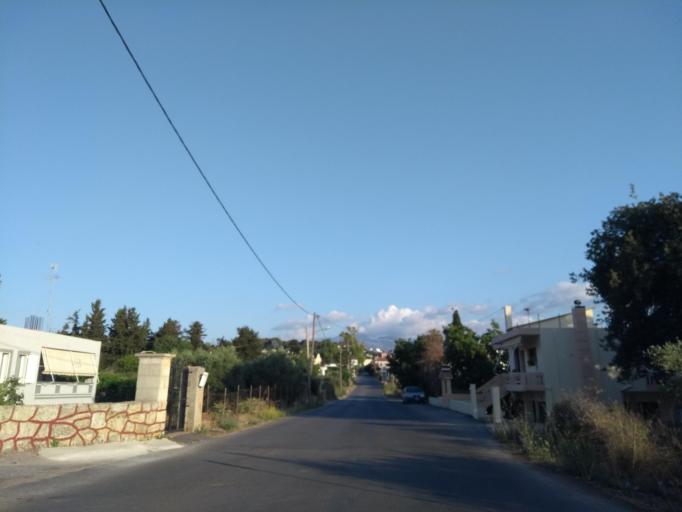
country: GR
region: Crete
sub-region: Nomos Chanias
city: Kalivai
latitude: 35.4131
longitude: 24.1953
